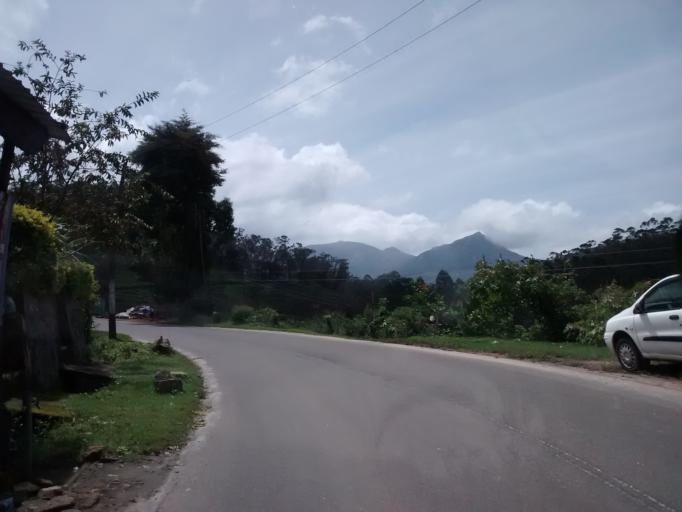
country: IN
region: Kerala
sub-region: Idukki
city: Munnar
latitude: 10.0953
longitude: 77.1002
